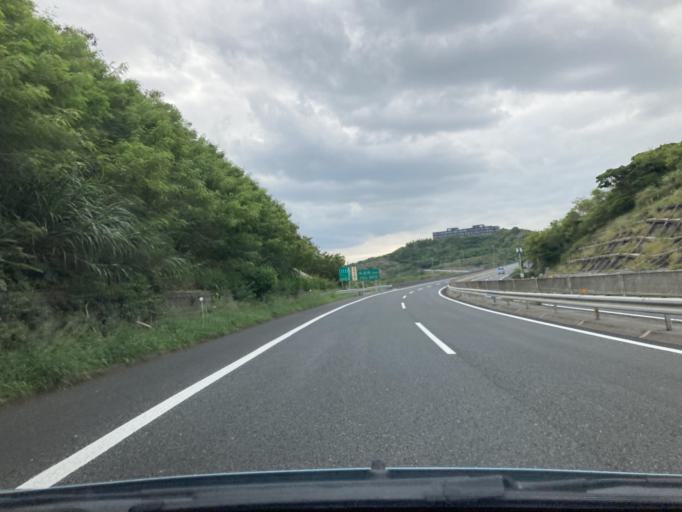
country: JP
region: Okinawa
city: Ginowan
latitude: 26.2150
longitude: 127.7380
